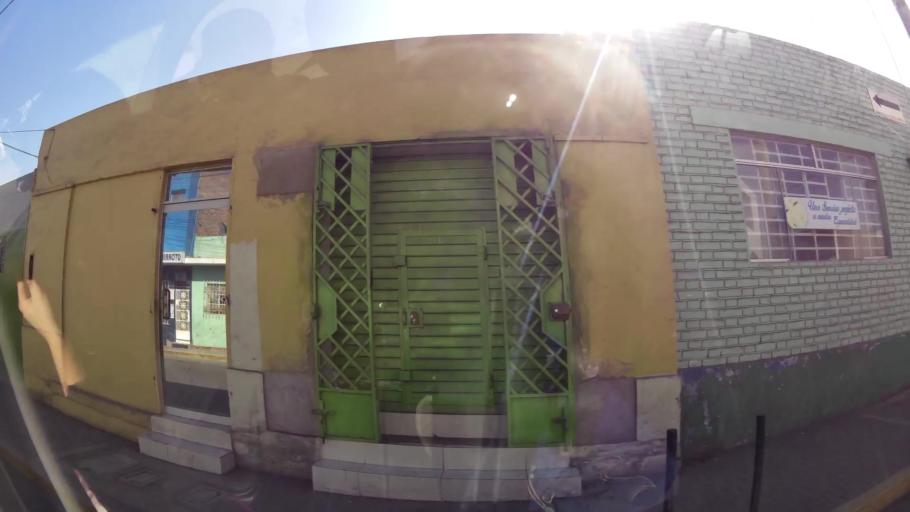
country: PE
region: Ica
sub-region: Provincia de Chincha
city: Chincha Alta
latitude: -13.4177
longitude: -76.1309
